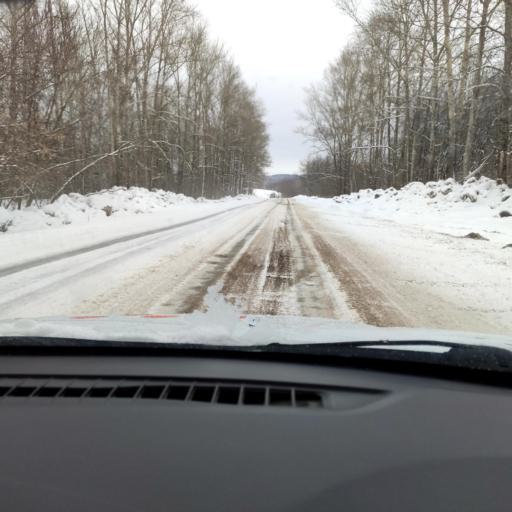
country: RU
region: Bashkortostan
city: Blagoveshchensk
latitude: 55.0497
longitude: 56.0130
